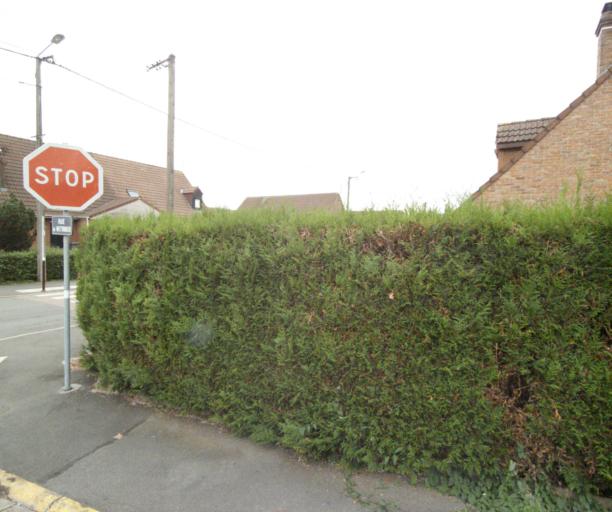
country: FR
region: Nord-Pas-de-Calais
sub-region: Departement du Nord
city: Fretin
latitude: 50.5571
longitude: 3.1290
